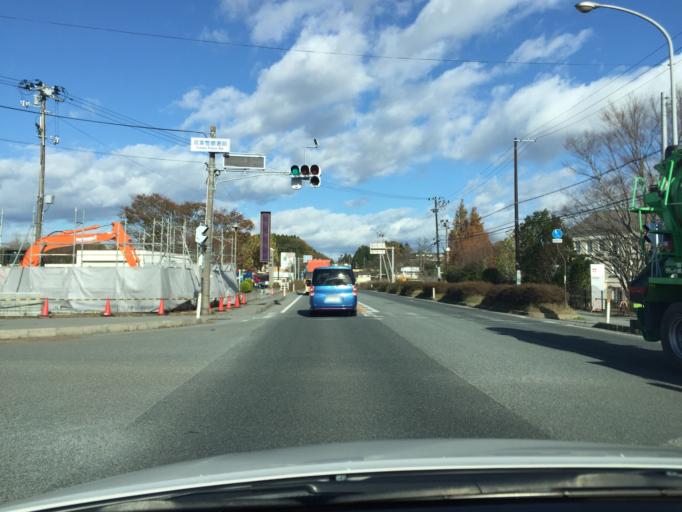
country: JP
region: Fukushima
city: Namie
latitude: 37.3401
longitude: 141.0135
